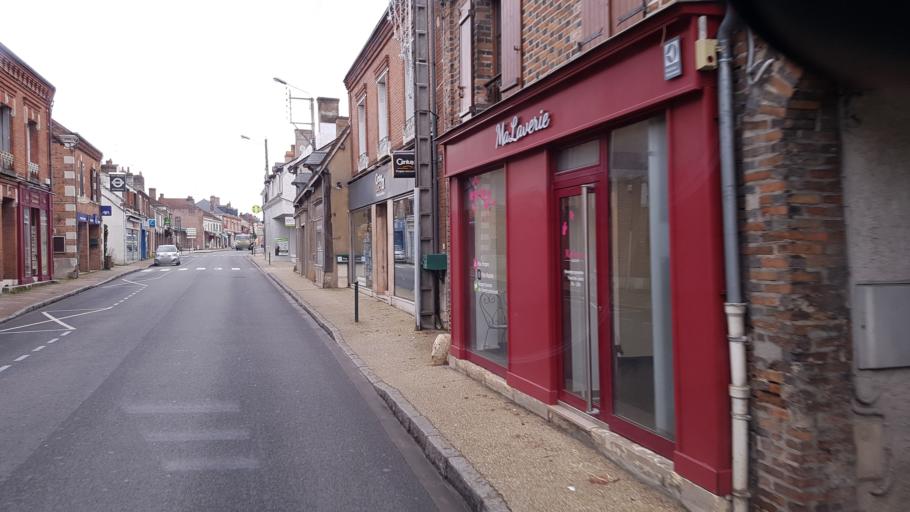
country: FR
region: Centre
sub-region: Departement du Loiret
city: La Ferte-Saint-Aubin
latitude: 47.7240
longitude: 1.9412
